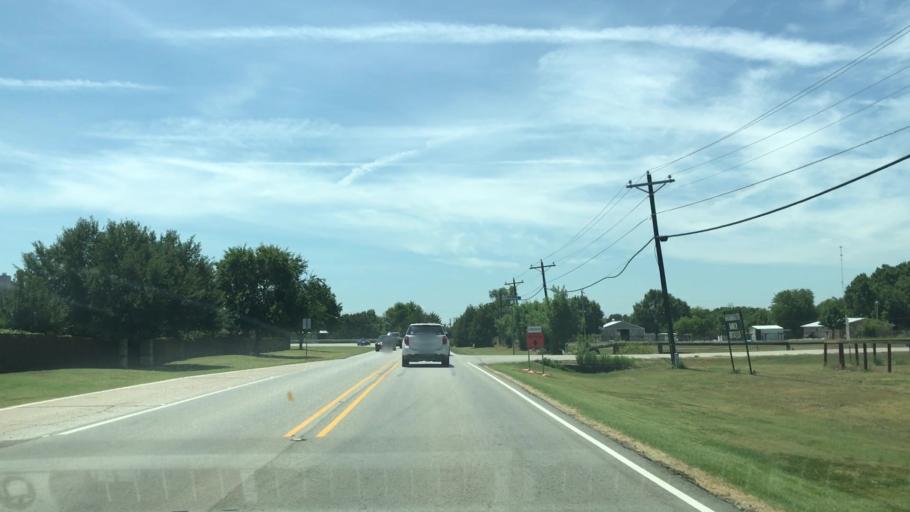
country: US
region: Texas
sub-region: Collin County
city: Lucas
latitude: 33.0772
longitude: -96.5768
